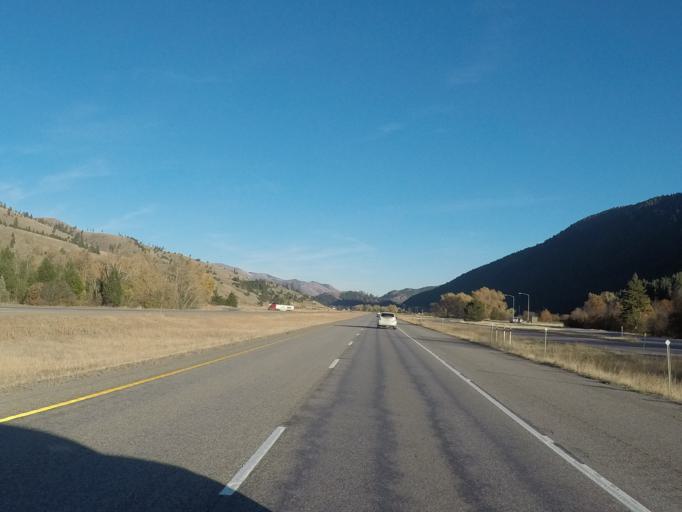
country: US
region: Montana
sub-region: Missoula County
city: Clinton
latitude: 46.7270
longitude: -113.6435
